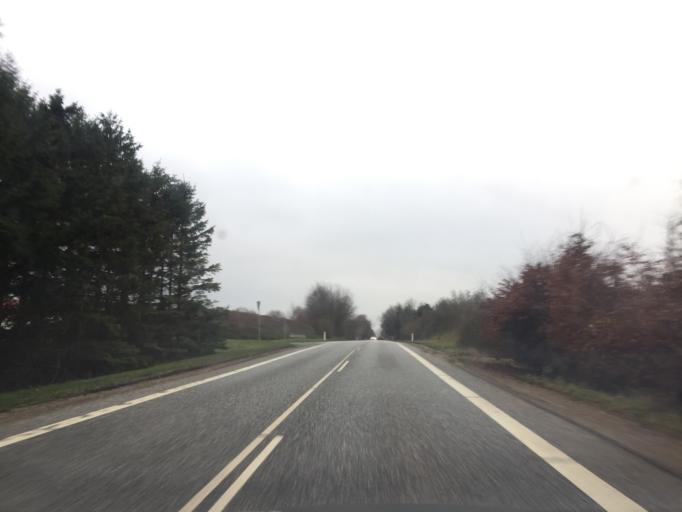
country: DK
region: South Denmark
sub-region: Svendborg Kommune
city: Svendborg
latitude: 55.1094
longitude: 10.6460
